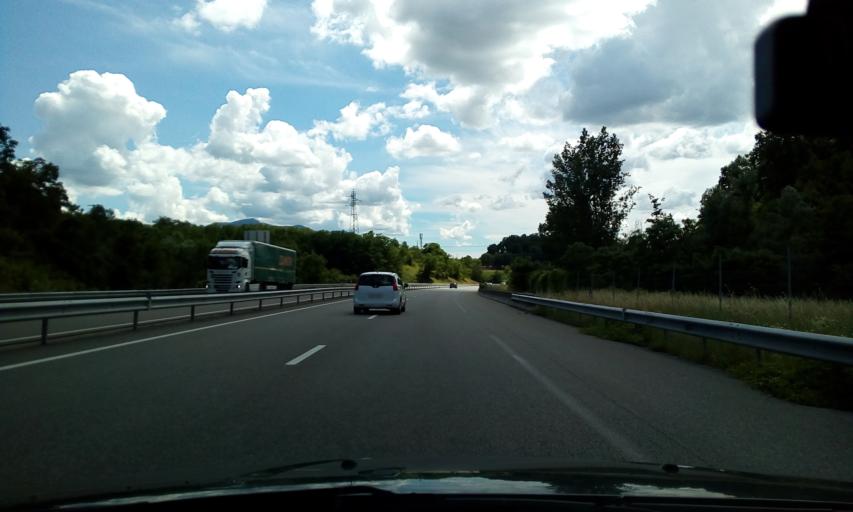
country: FR
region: Rhone-Alpes
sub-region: Departement de l'Isere
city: Saint-Hilaire-du-Rosier
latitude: 45.1103
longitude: 5.2559
